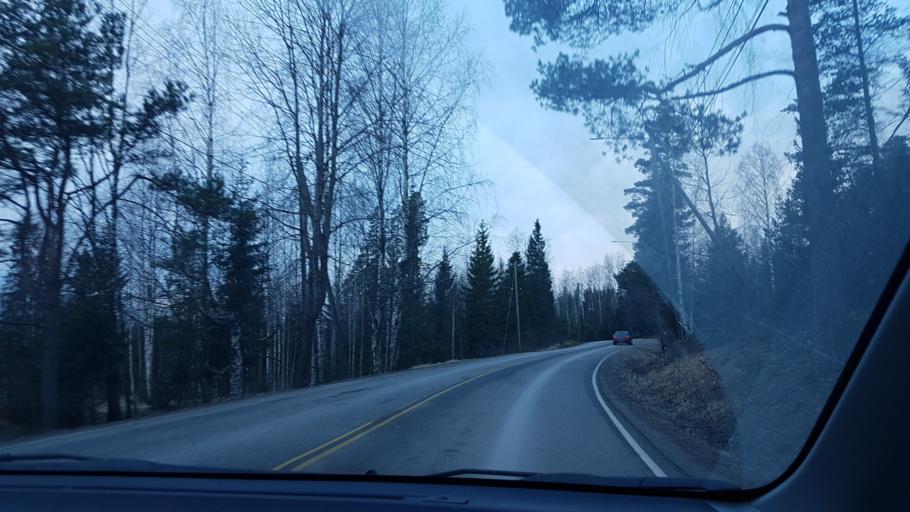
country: FI
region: Uusimaa
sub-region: Helsinki
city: Kauniainen
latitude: 60.3441
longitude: 24.7245
